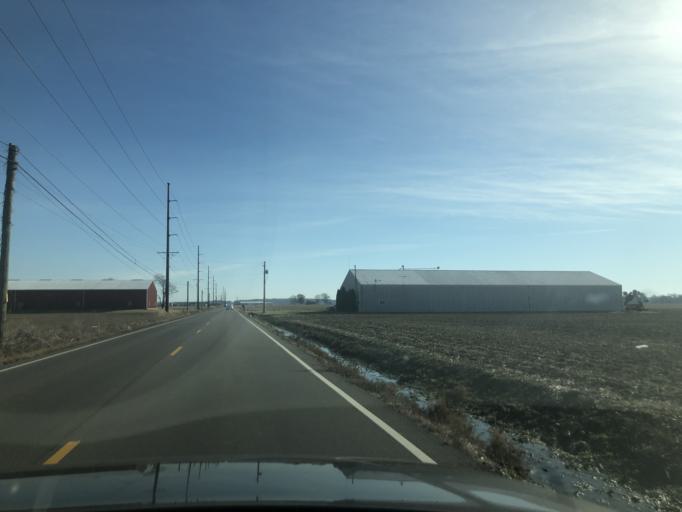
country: US
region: Indiana
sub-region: Vanderburgh County
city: Melody Hill
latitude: 37.9912
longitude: -87.4571
